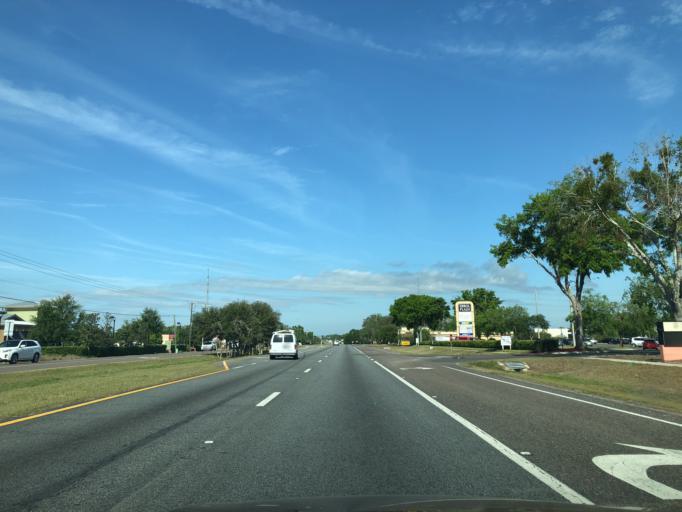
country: US
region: Florida
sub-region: Orange County
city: Apopka
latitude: 28.6866
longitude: -81.5365
